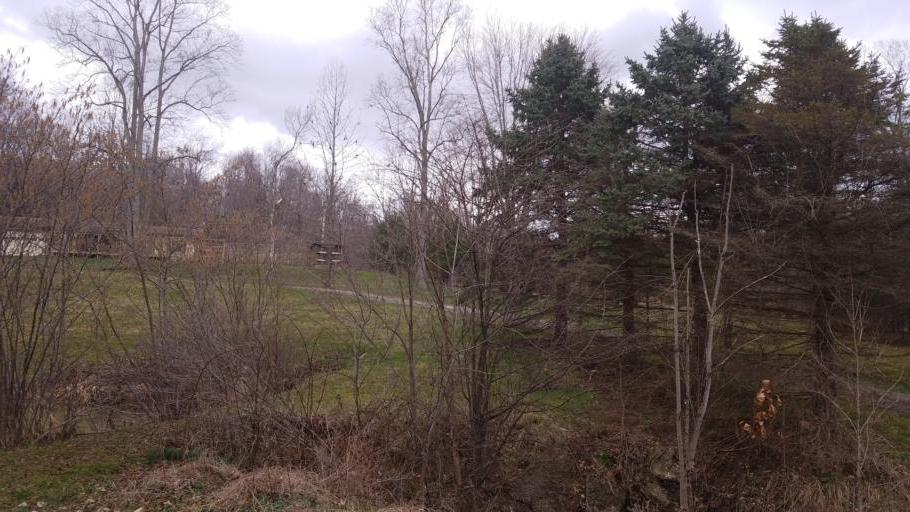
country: US
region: Ohio
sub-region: Muskingum County
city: Frazeysburg
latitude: 40.1464
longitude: -82.2690
